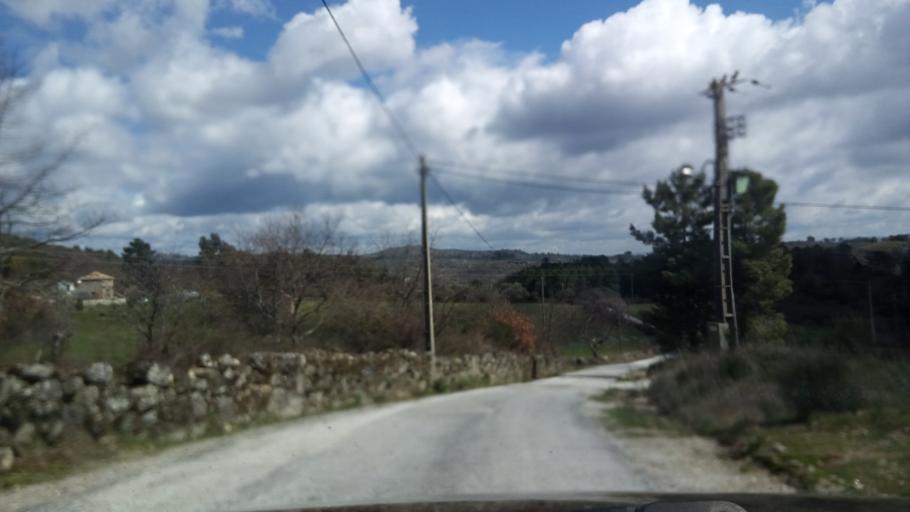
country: PT
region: Guarda
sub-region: Fornos de Algodres
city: Fornos de Algodres
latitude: 40.6318
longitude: -7.5222
